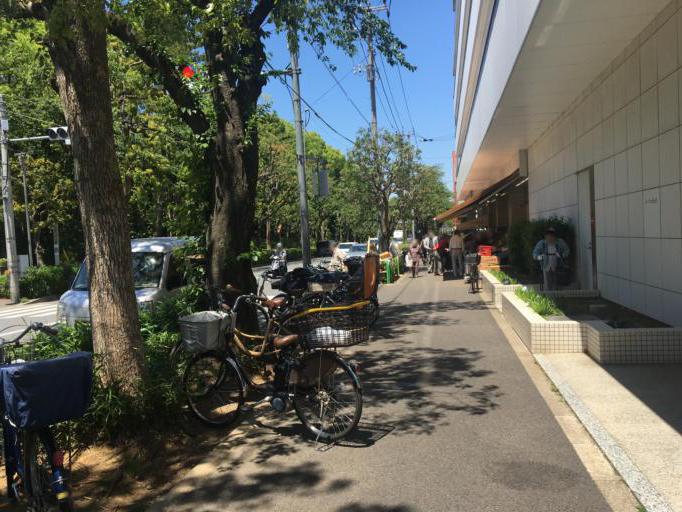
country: JP
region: Saitama
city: Wako
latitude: 35.7663
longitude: 139.6357
